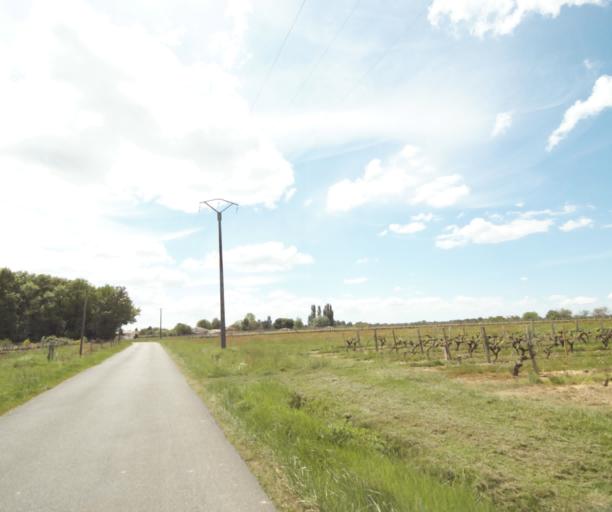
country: FR
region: Poitou-Charentes
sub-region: Departement de la Charente-Maritime
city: Burie
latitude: 45.7513
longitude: -0.4455
